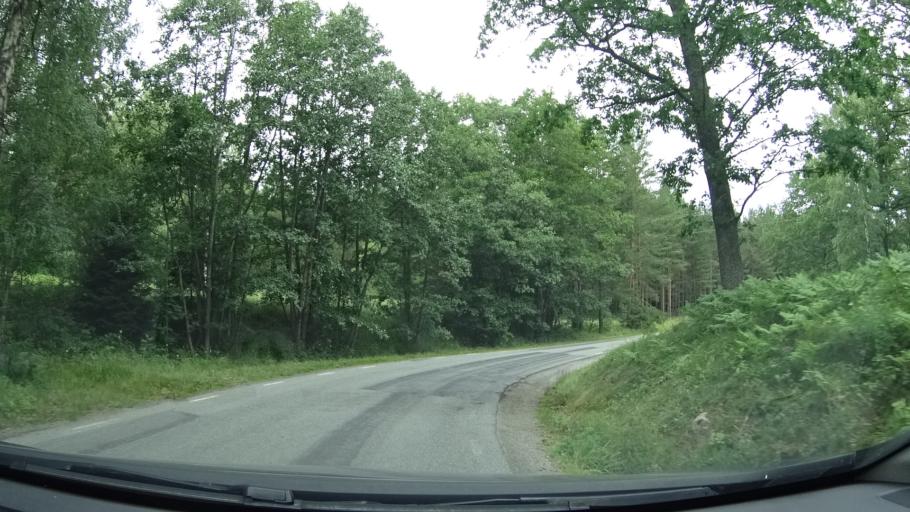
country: SE
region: Stockholm
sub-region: Varmdo Kommun
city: Mortnas
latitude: 59.3682
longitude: 18.4645
